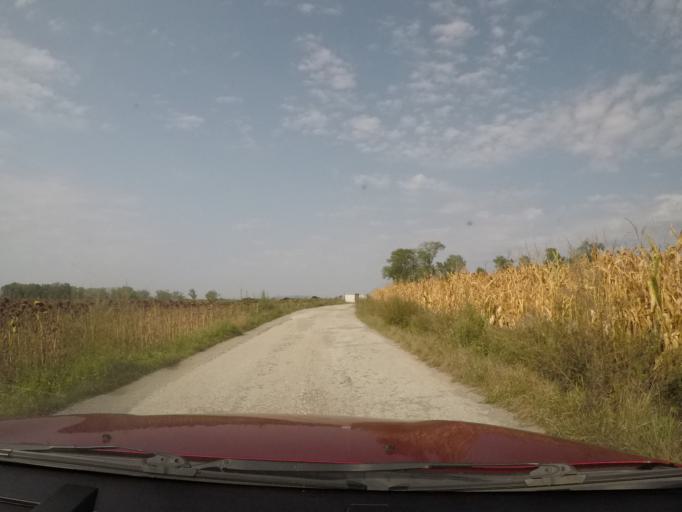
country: SK
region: Kosicky
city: Moldava nad Bodvou
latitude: 48.5873
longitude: 21.0072
